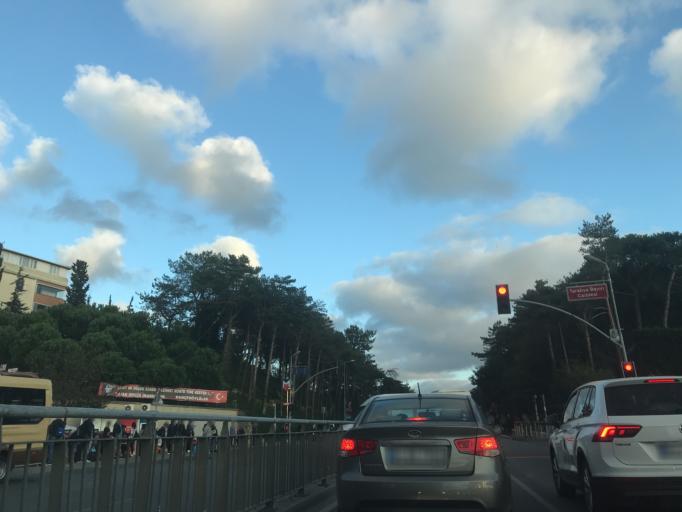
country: TR
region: Istanbul
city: Sisli
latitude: 41.1401
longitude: 29.0307
